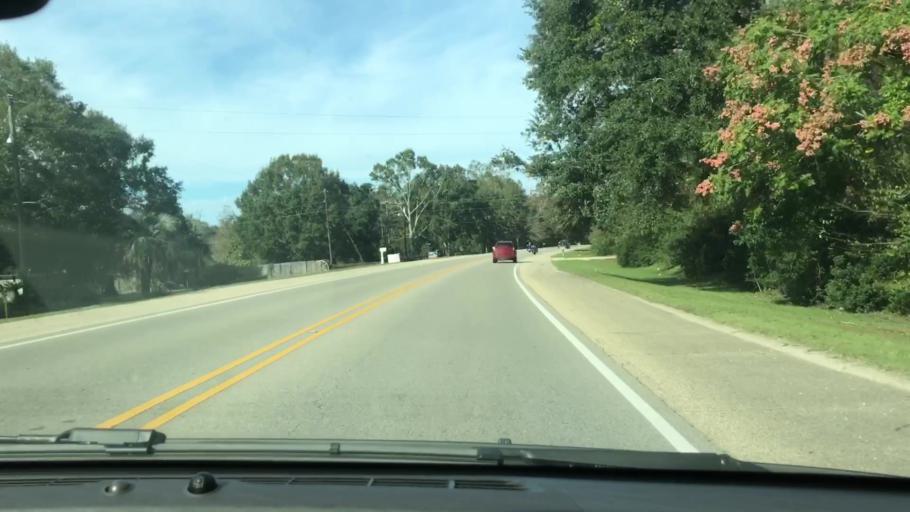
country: US
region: Louisiana
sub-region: Saint Tammany Parish
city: Pearl River
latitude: 30.4259
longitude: -89.7877
